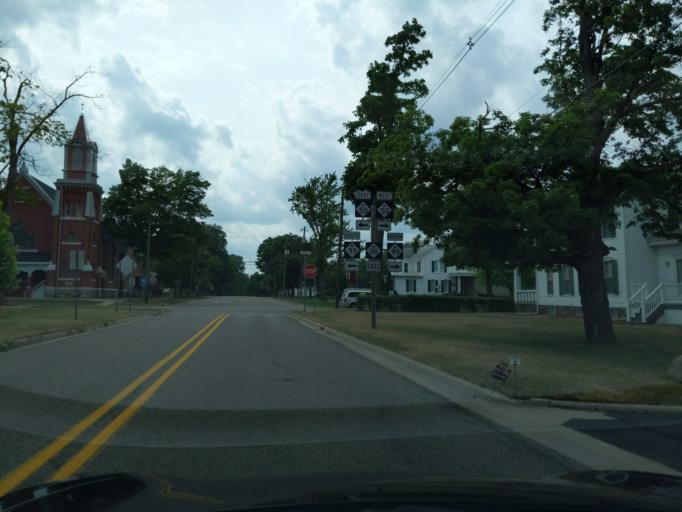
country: US
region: Michigan
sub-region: Eaton County
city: Eaton Rapids
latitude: 42.5077
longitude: -84.6554
